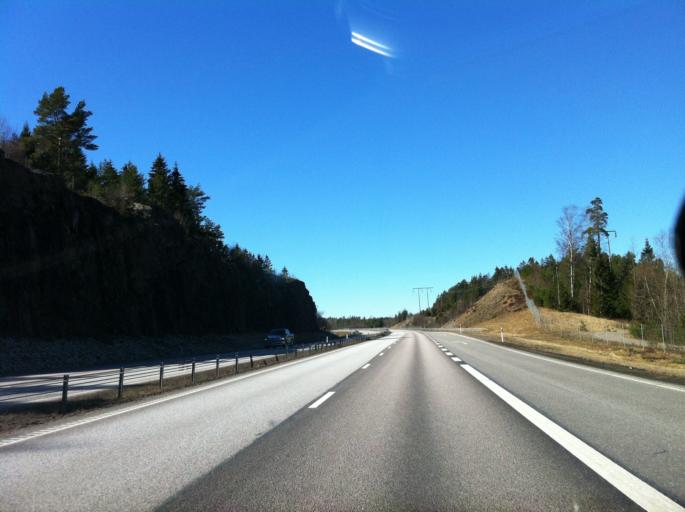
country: SE
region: Vaestra Goetaland
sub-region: Vanersborgs Kommun
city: Vanersborg
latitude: 58.3785
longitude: 12.3338
